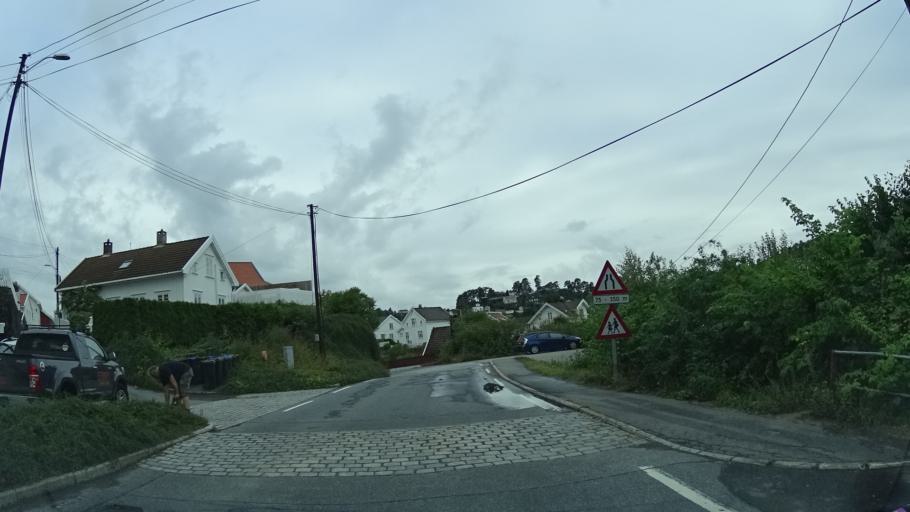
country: NO
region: Aust-Agder
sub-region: Arendal
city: Arendal
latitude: 58.4510
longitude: 8.7576
